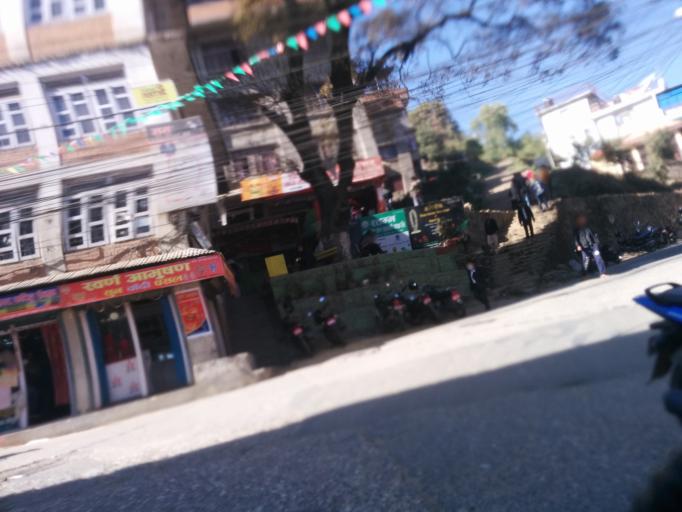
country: NP
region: Central Region
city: Kirtipur
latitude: 27.6771
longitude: 85.2810
